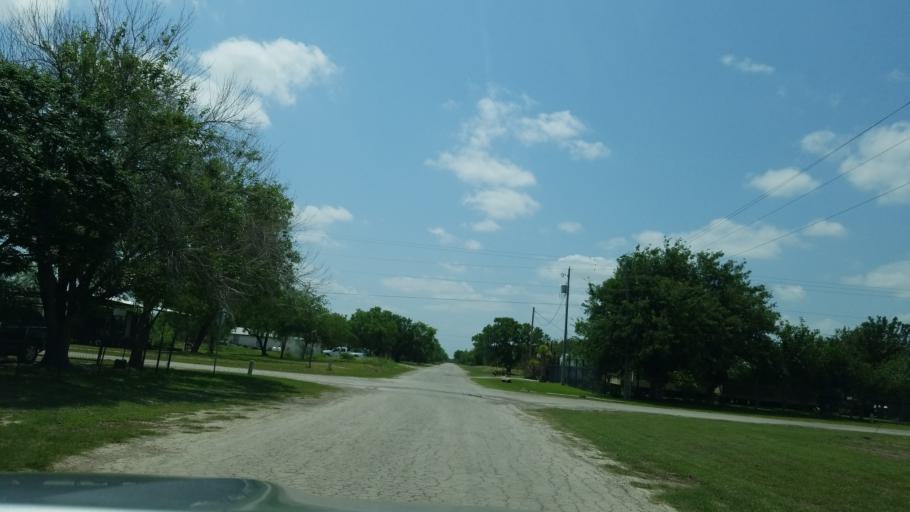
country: US
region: Texas
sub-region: Zavala County
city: La Pryor
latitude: 28.9420
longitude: -99.8413
